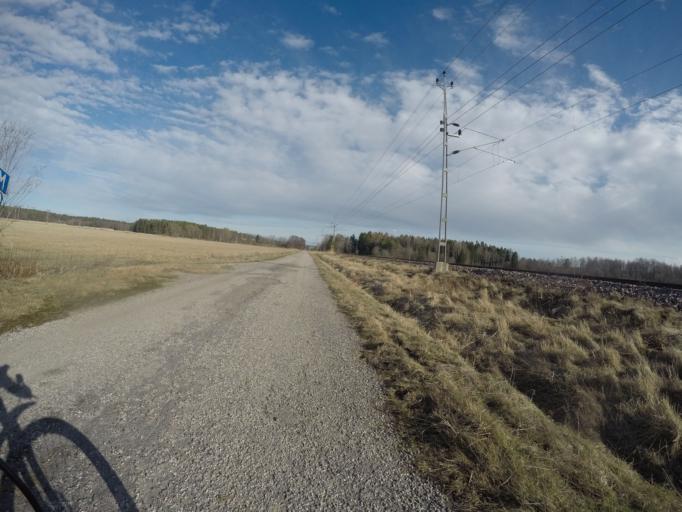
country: SE
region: Vaestmanland
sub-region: Kungsors Kommun
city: Kungsoer
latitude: 59.4232
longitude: 16.1548
